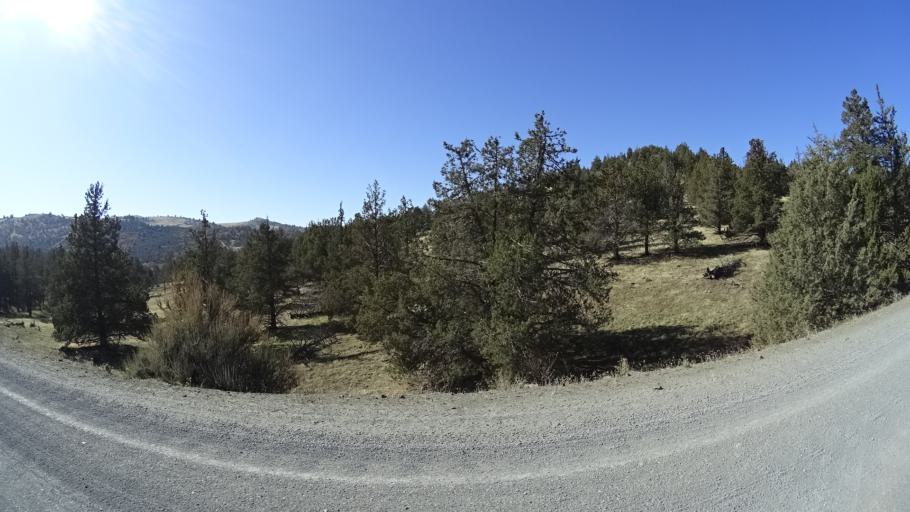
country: US
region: California
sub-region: Siskiyou County
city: Montague
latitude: 41.8045
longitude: -122.3708
